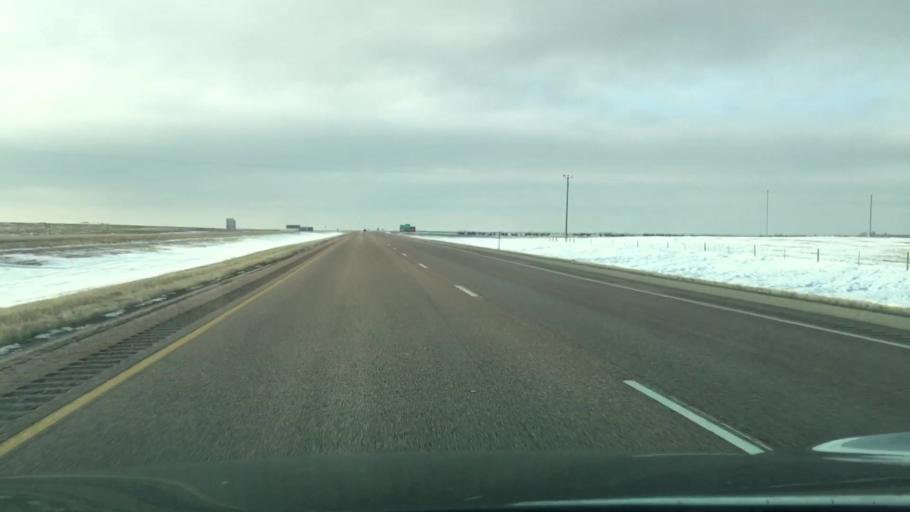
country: US
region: South Dakota
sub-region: Buffalo County
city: Fort Thompson
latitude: 43.8571
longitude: -99.5845
